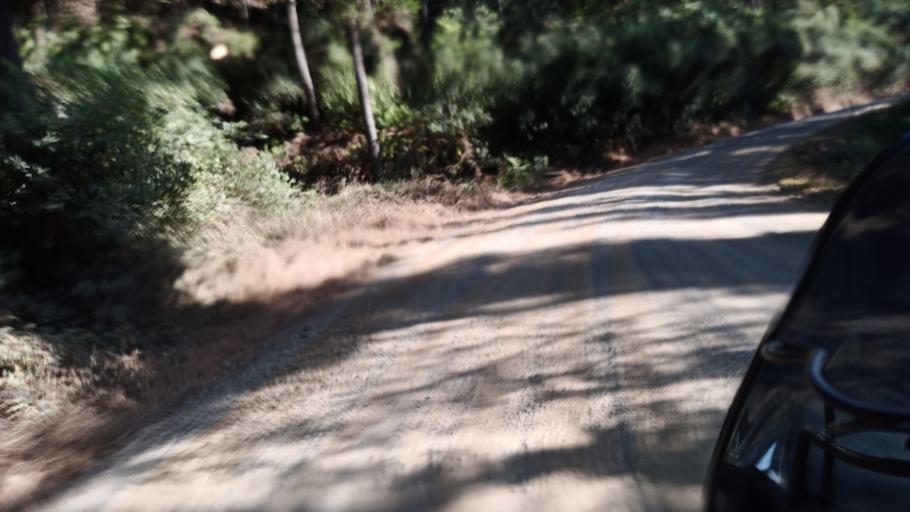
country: NZ
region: Hawke's Bay
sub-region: Wairoa District
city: Wairoa
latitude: -38.9283
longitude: 177.2168
